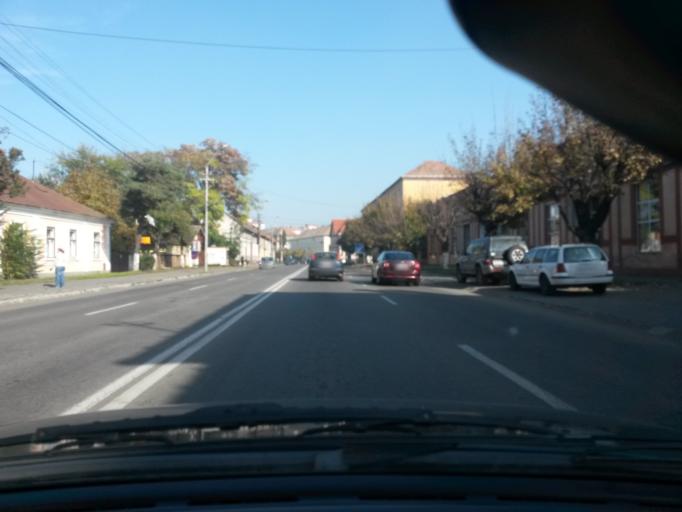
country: RO
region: Mures
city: Targu-Mures
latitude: 46.5363
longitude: 24.5561
